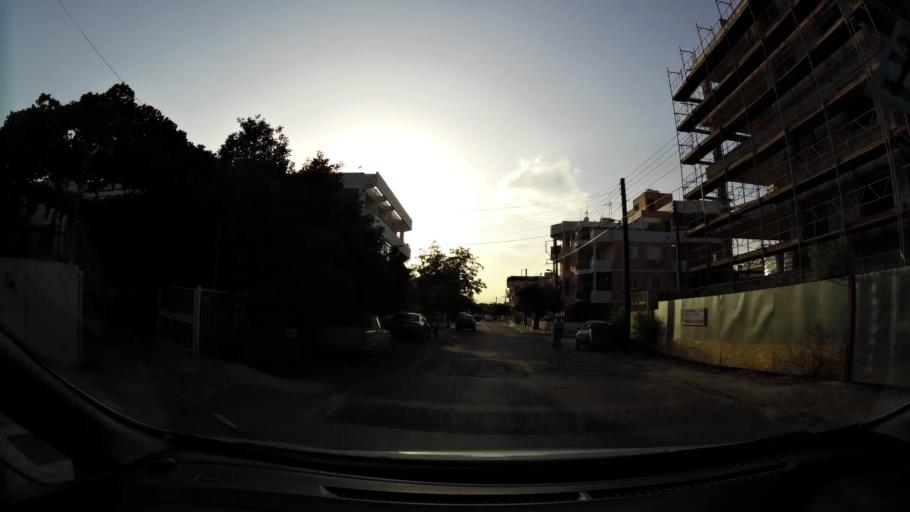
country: CY
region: Lefkosia
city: Nicosia
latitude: 35.1662
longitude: 33.3331
